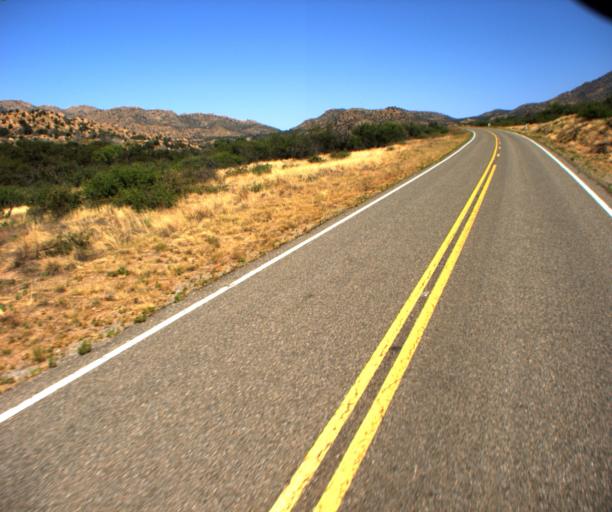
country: US
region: Arizona
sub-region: Graham County
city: Swift Trail Junction
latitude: 32.5654
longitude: -109.8029
